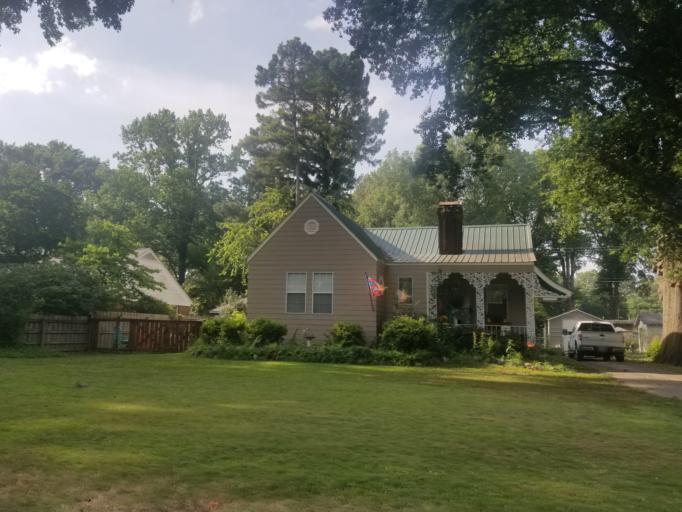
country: US
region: Arkansas
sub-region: Cross County
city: Wynne
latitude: 35.2253
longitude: -90.7805
